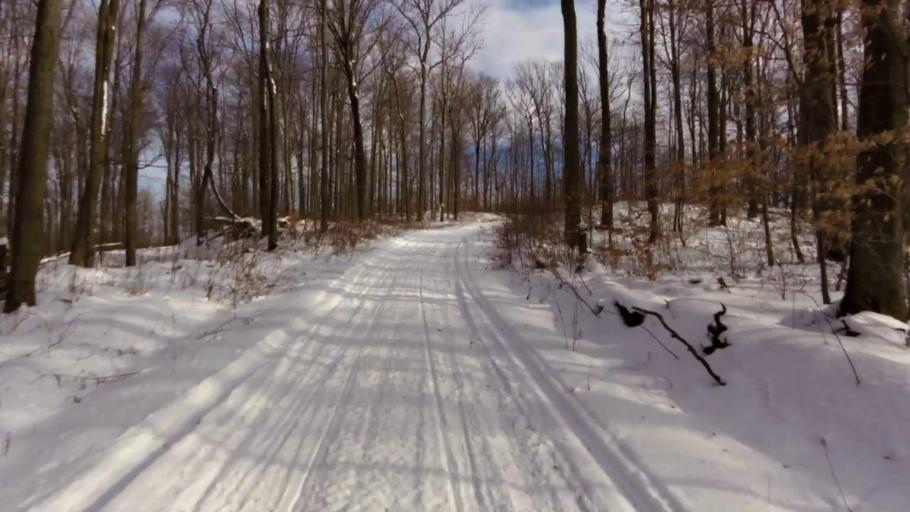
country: US
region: Pennsylvania
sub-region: McKean County
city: Foster Brook
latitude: 42.0067
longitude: -78.5900
